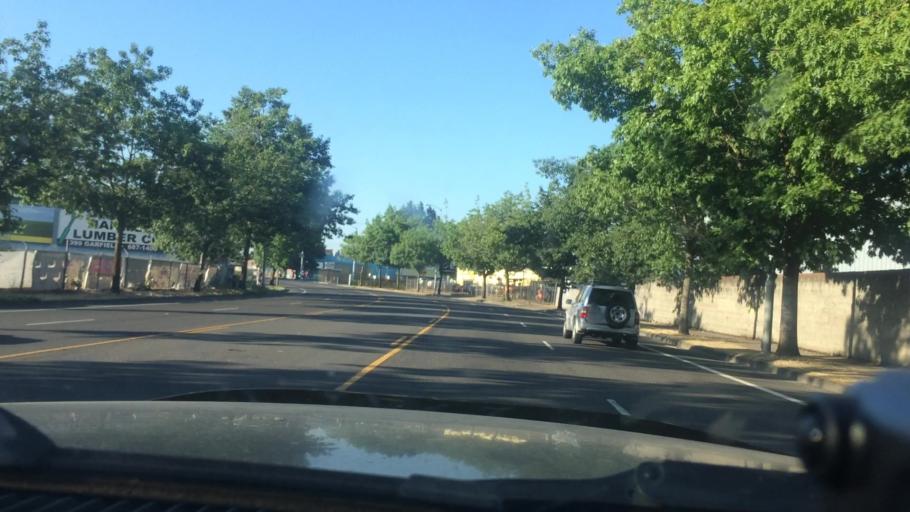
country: US
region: Oregon
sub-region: Lane County
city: Eugene
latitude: 44.0560
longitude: -123.1180
